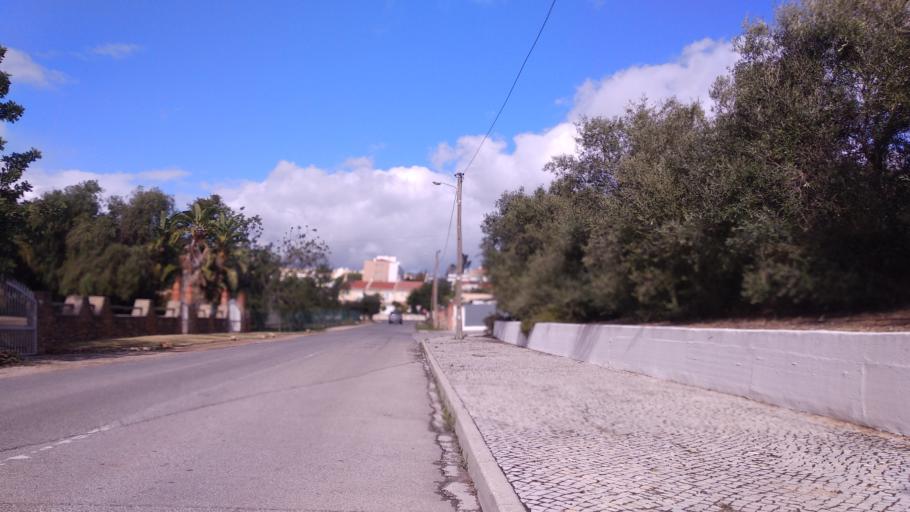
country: PT
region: Faro
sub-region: Sao Bras de Alportel
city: Sao Bras de Alportel
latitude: 37.1490
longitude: -7.8945
